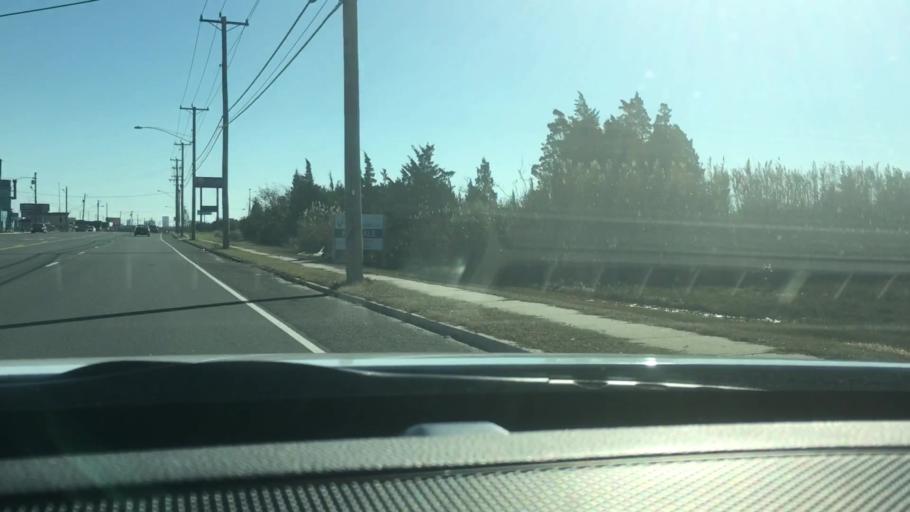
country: US
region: New Jersey
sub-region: Atlantic County
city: Pleasantville
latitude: 39.3839
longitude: -74.5036
